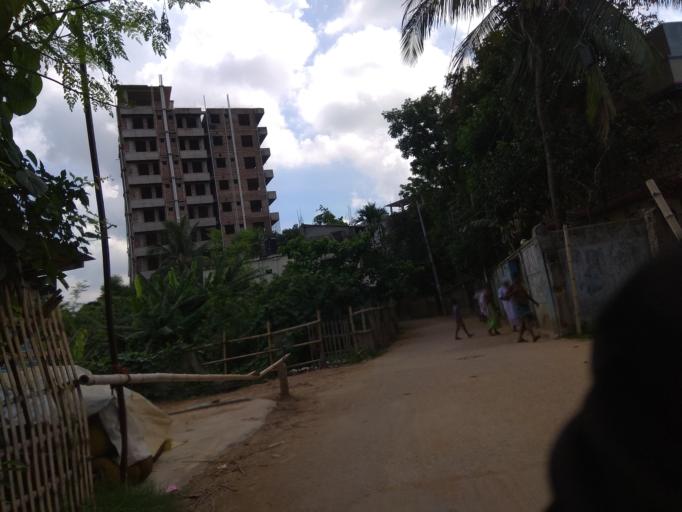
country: BD
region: Dhaka
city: Tungi
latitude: 23.8223
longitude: 90.3859
